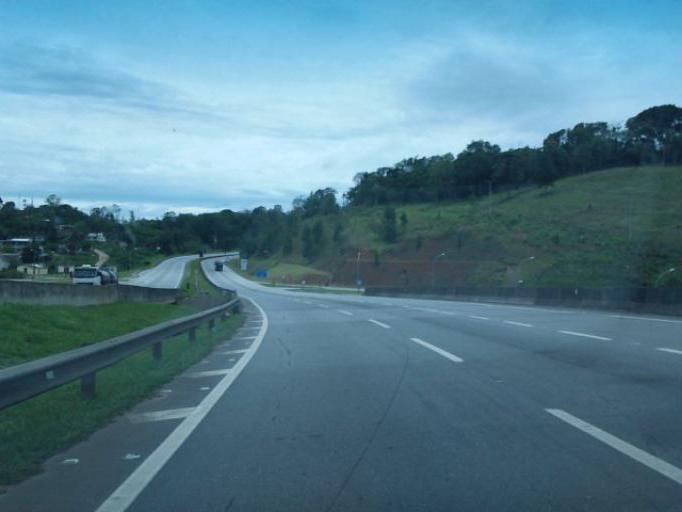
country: BR
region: Sao Paulo
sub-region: Juquitiba
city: Juquitiba
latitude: -24.0047
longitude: -47.1585
